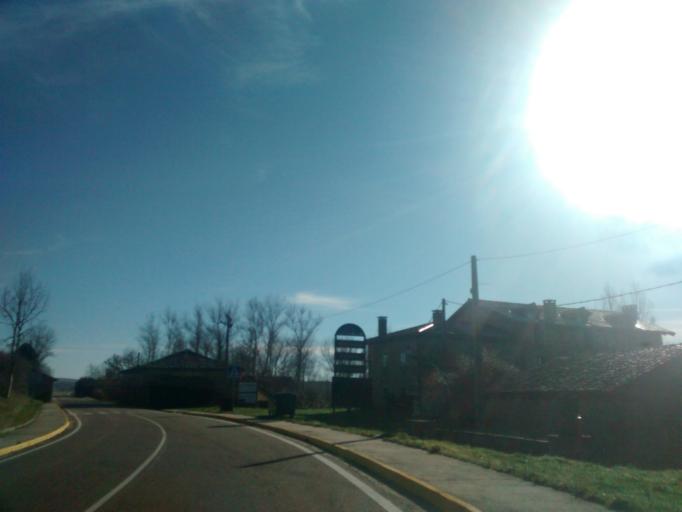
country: ES
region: Castille and Leon
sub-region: Provincia de Burgos
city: Arija
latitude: 42.9825
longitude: -3.8138
